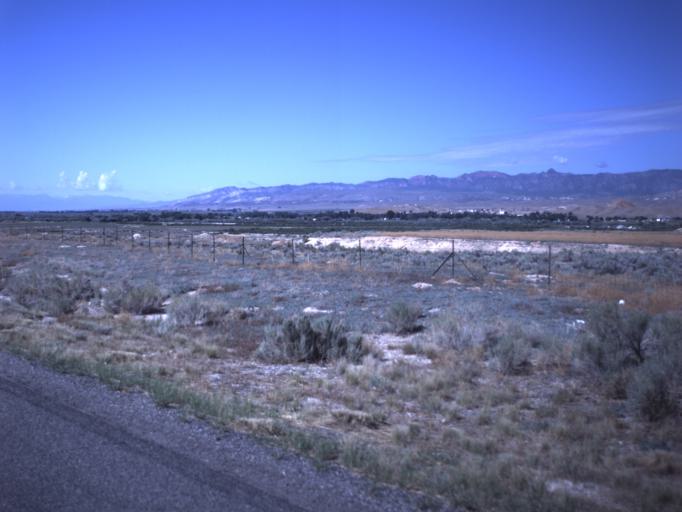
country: US
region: Utah
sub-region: Sevier County
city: Salina
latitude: 39.0204
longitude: -111.8330
